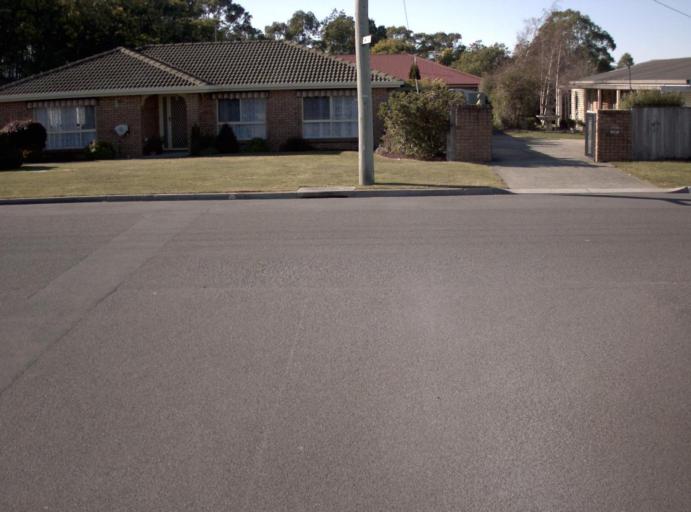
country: AU
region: Tasmania
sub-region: Launceston
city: Summerhill
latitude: -41.4671
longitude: 147.1338
